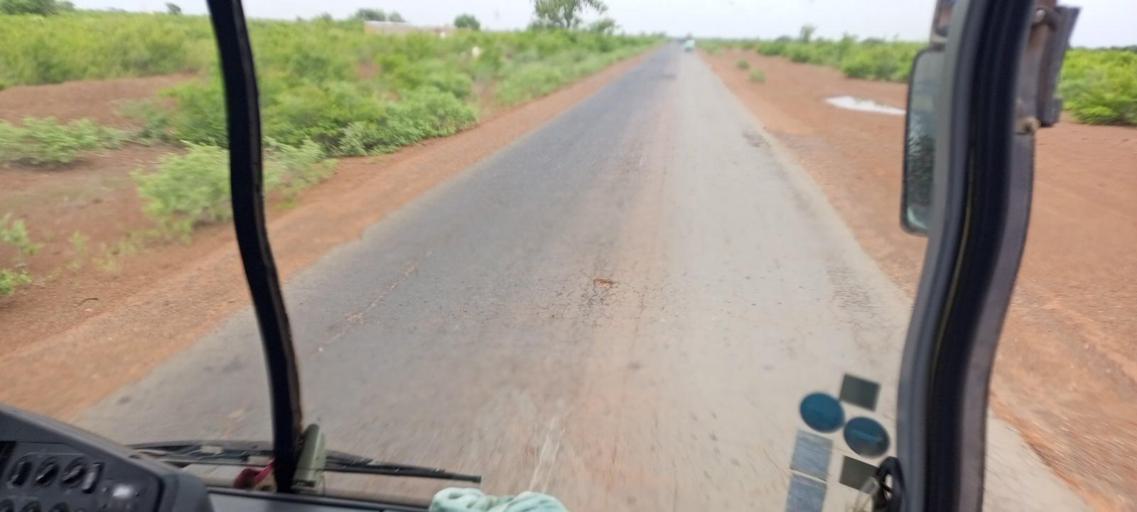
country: ML
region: Segou
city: Bla
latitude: 12.7573
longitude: -5.7365
